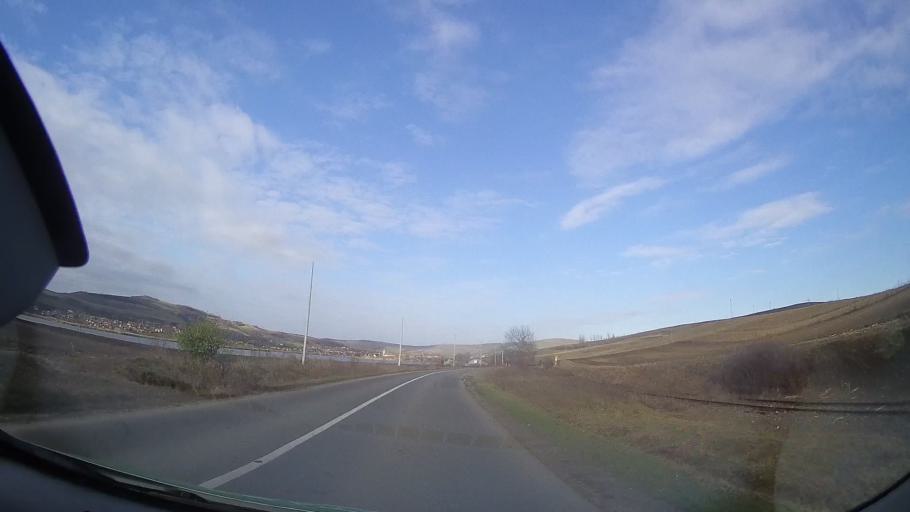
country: RO
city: Barza
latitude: 46.5681
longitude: 24.0919
